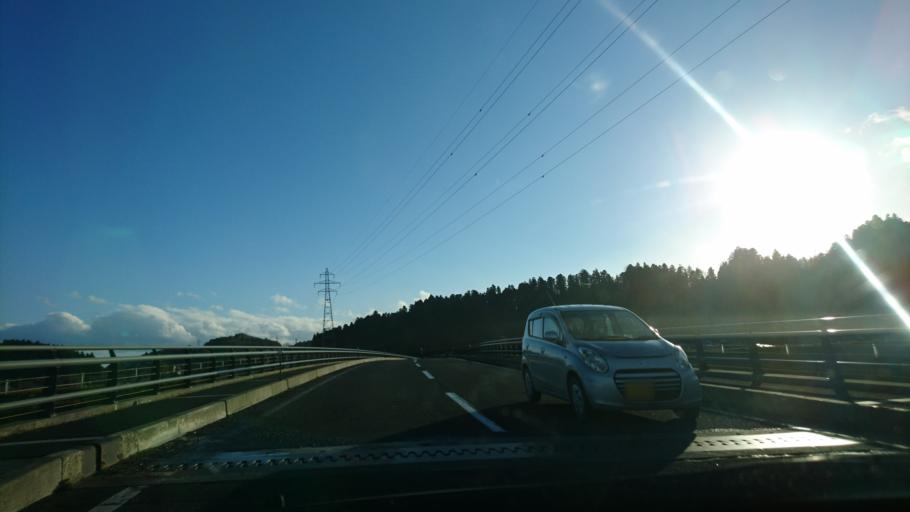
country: JP
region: Iwate
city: Ichinoseki
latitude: 39.0055
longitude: 141.1083
